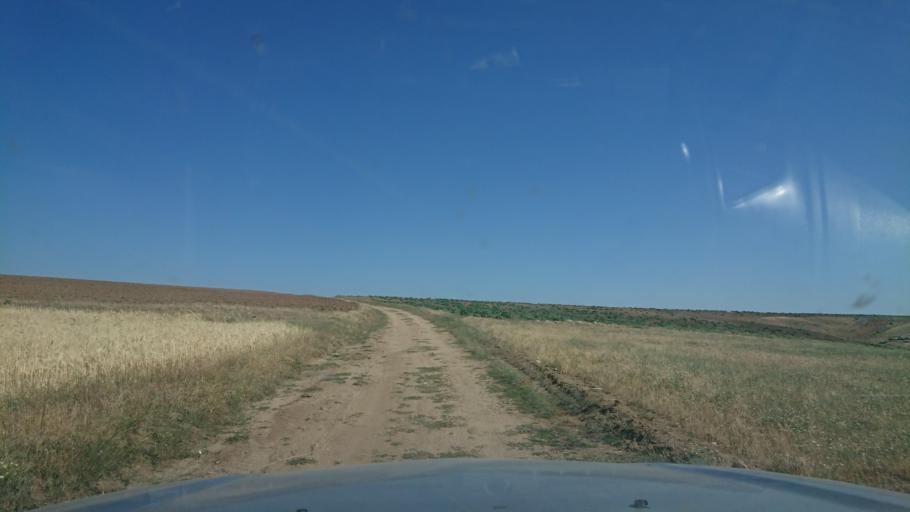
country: TR
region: Aksaray
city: Agacoren
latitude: 38.8467
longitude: 33.9179
